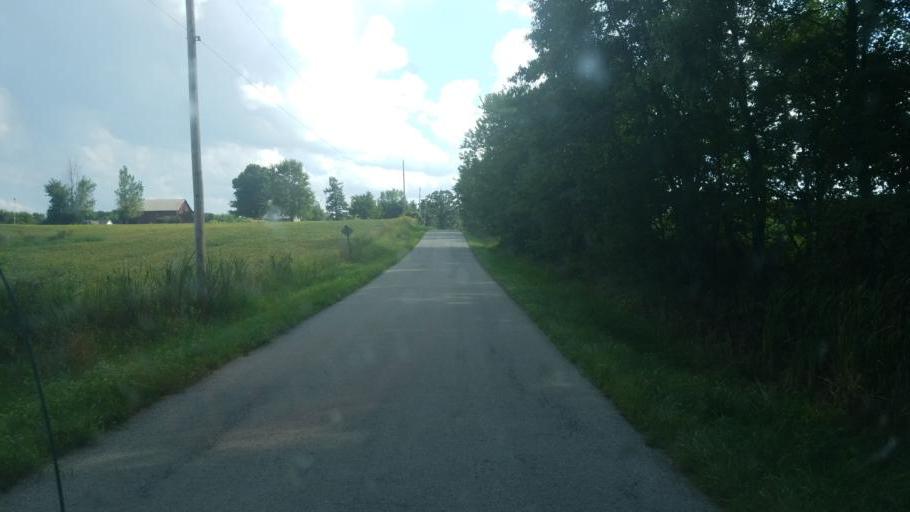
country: US
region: Ohio
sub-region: Huron County
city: Plymouth
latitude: 41.0078
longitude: -82.6509
